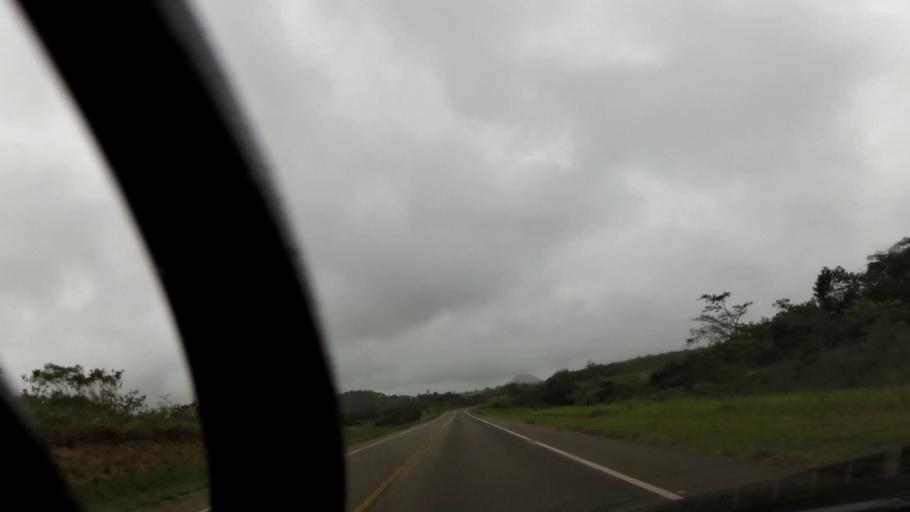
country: BR
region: Espirito Santo
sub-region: Guarapari
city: Guarapari
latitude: -20.7131
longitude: -40.5763
